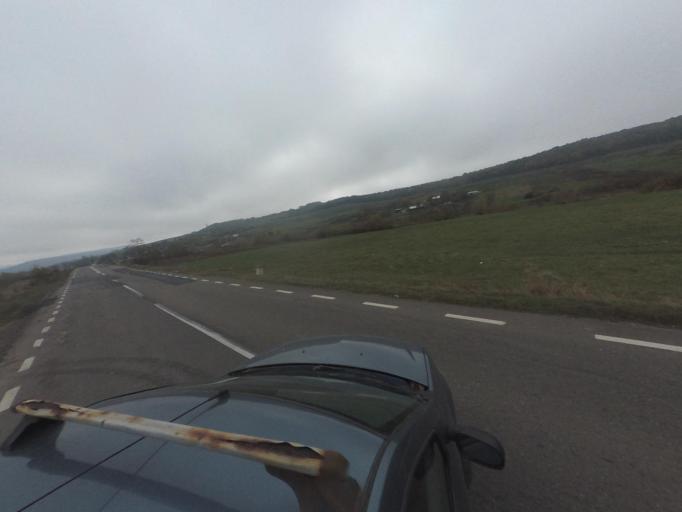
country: RO
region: Vaslui
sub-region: Comuna Bacesti
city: Bacesti
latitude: 46.8390
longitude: 27.2261
